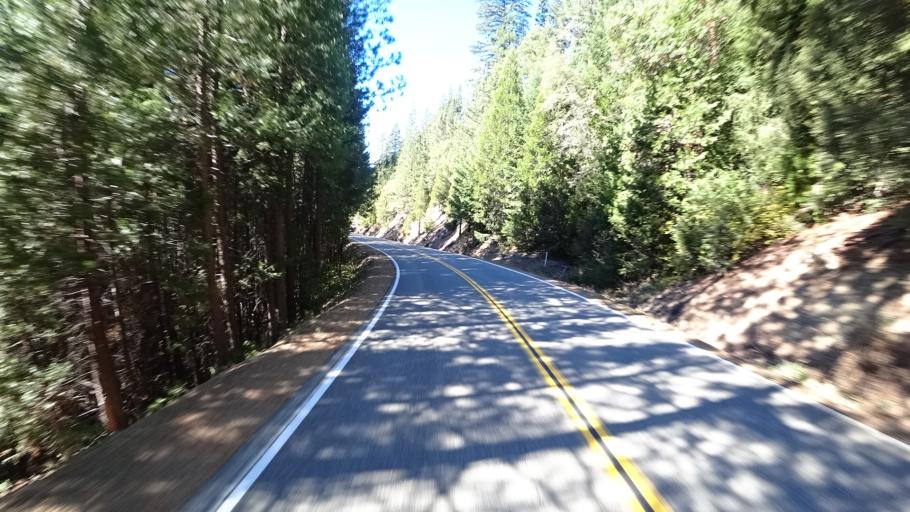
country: US
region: California
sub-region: Trinity County
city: Weaverville
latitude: 41.2258
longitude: -123.0047
